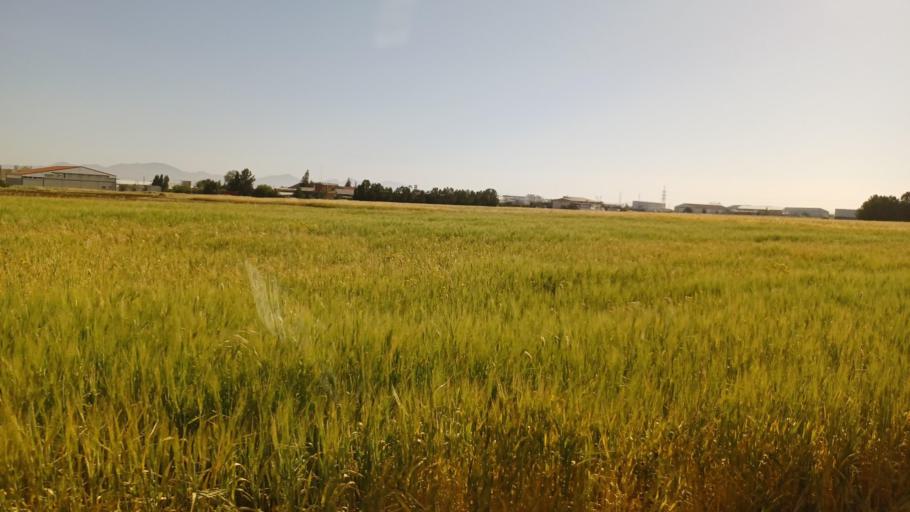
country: CY
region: Lefkosia
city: Kokkinotrimithia
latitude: 35.1459
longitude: 33.2201
